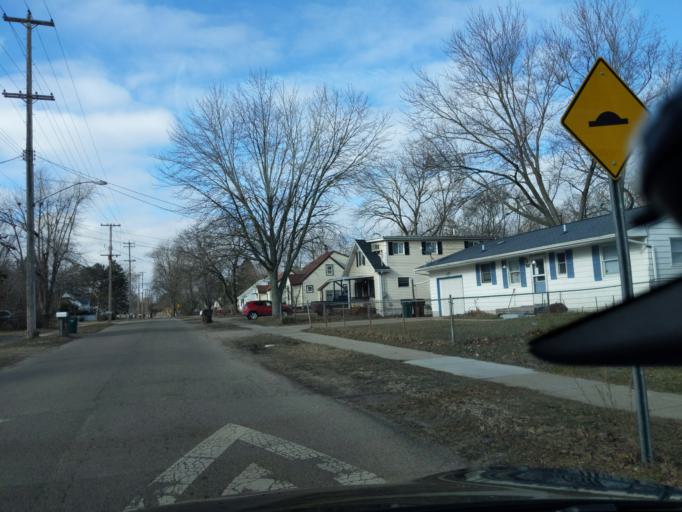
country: US
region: Michigan
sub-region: Ingham County
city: Lansing
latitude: 42.6930
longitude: -84.5734
